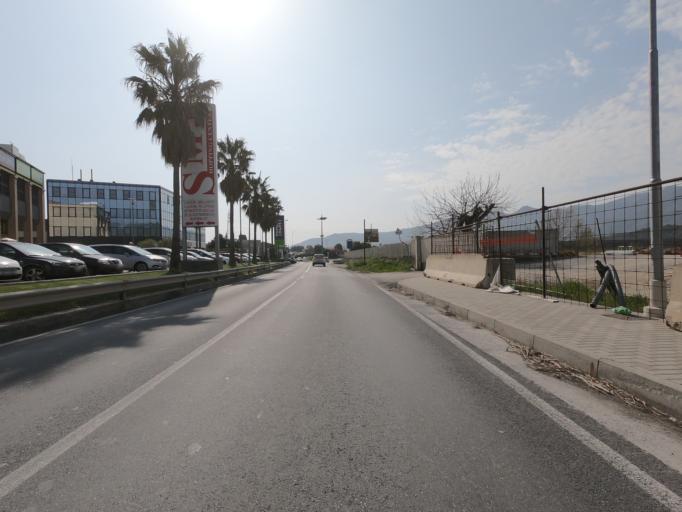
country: IT
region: Liguria
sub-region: Provincia di Savona
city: Cisano
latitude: 44.0695
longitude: 8.1692
